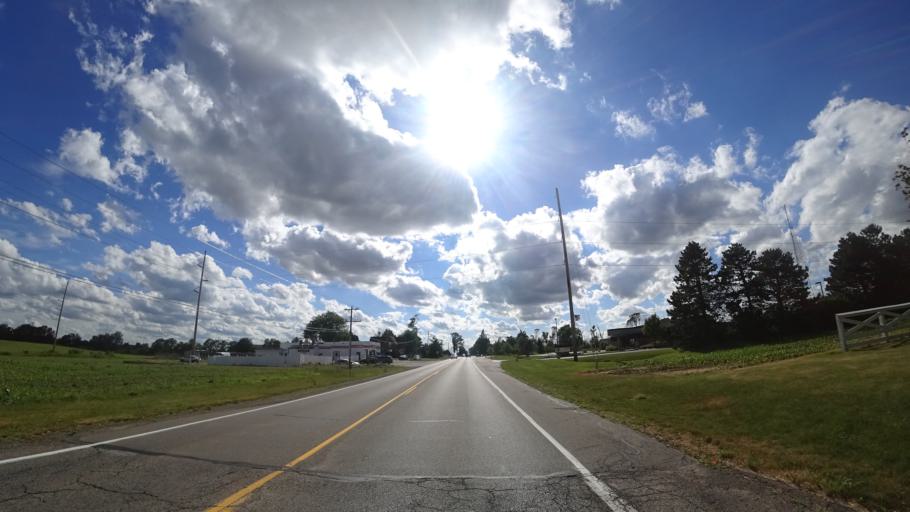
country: US
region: Michigan
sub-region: Ionia County
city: Portland
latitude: 42.8715
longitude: -84.9168
